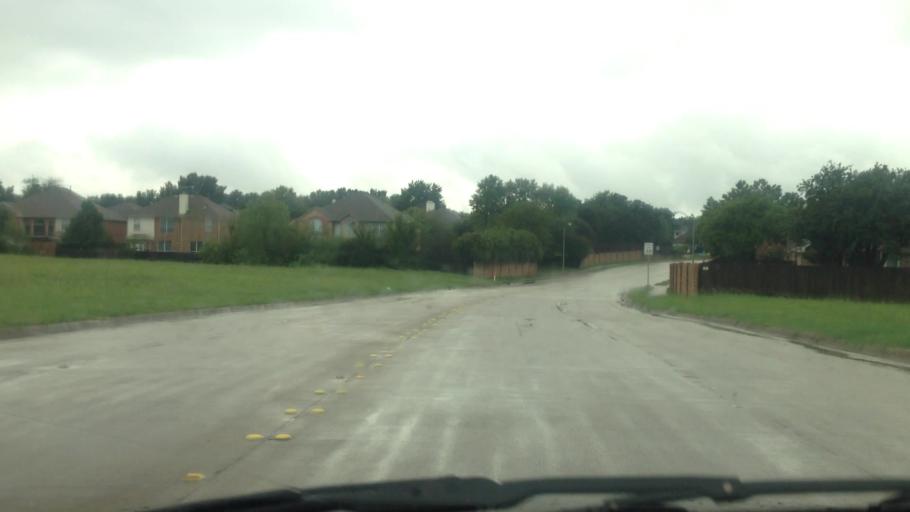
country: US
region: Texas
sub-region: Tarrant County
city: Colleyville
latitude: 32.8914
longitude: -97.2037
